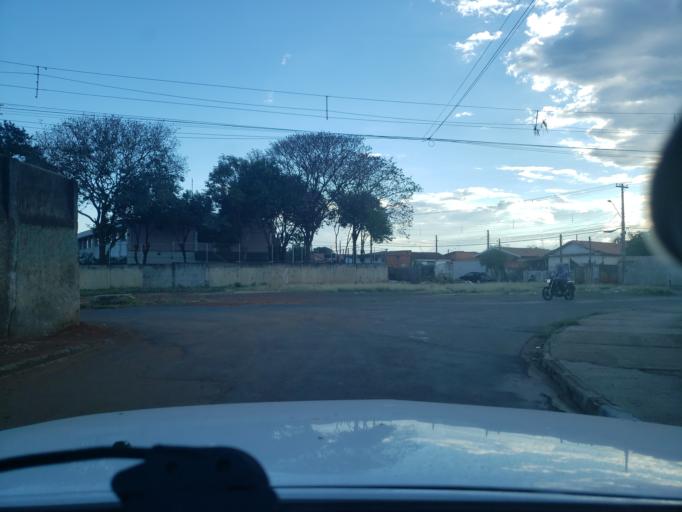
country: BR
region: Sao Paulo
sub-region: Moji-Guacu
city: Mogi-Gaucu
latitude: -22.3347
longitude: -46.9323
